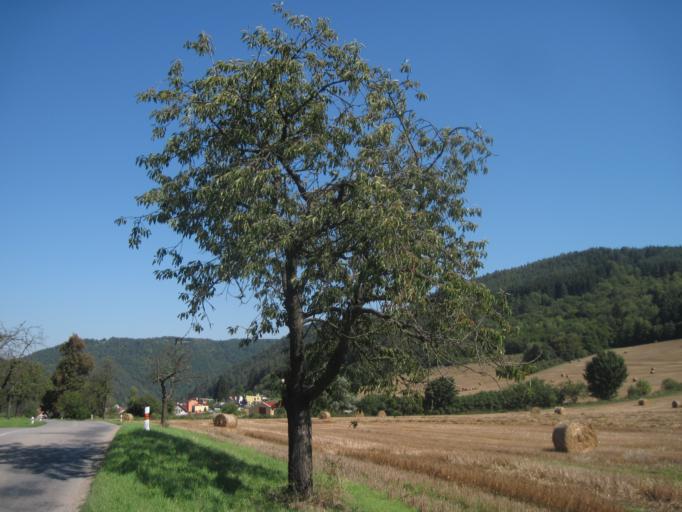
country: CZ
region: South Moravian
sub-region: Okres Brno-Venkov
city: Nedvedice
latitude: 49.4146
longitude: 16.3518
